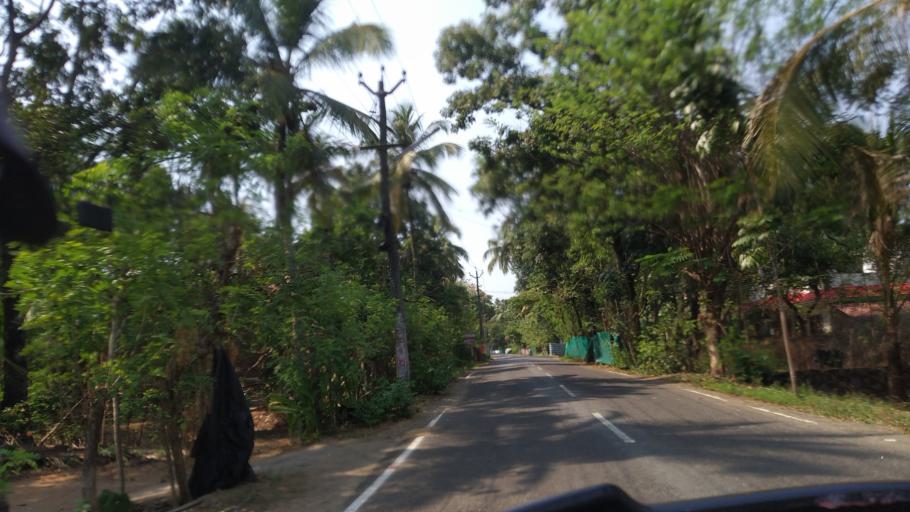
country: IN
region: Kerala
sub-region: Thrissur District
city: Thanniyam
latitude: 10.3620
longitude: 76.1083
